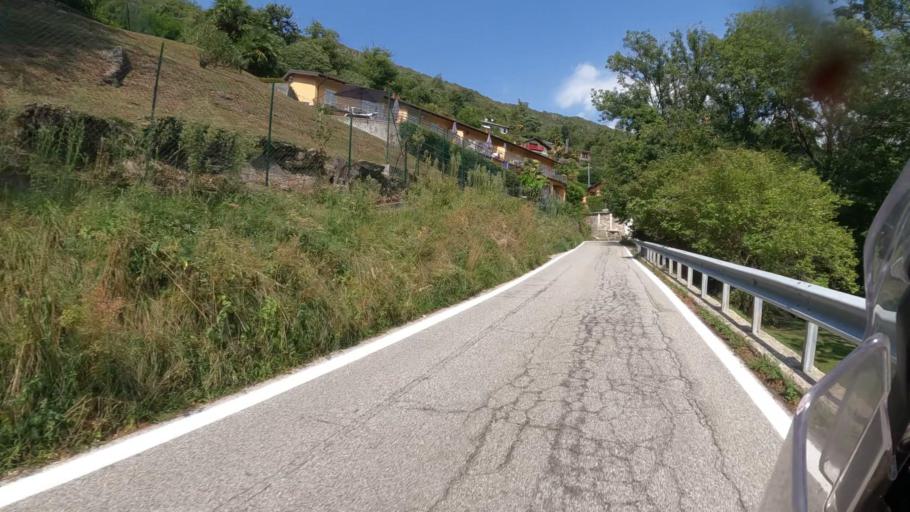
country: IT
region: Lombardy
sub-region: Provincia di Varese
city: Maccagno
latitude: 46.0487
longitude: 8.7503
